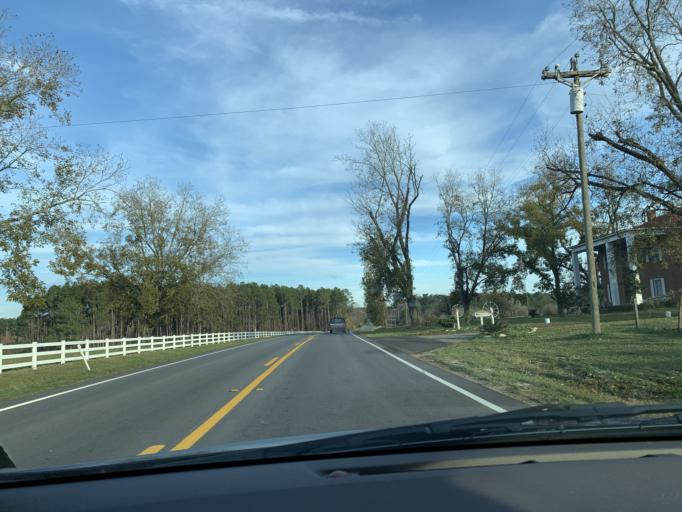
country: US
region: Georgia
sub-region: Irwin County
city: Ocilla
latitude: 31.5927
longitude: -83.2095
